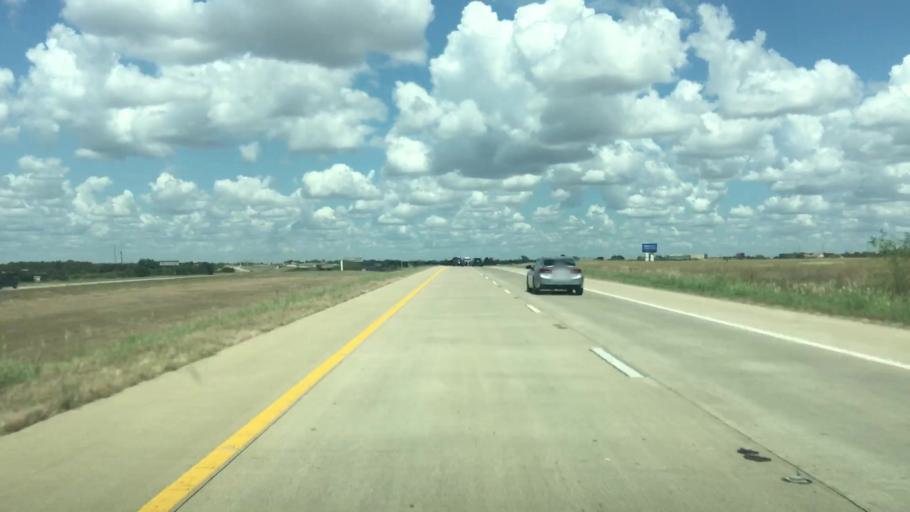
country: US
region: Texas
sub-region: Williamson County
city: Hutto
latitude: 30.5507
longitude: -97.5765
